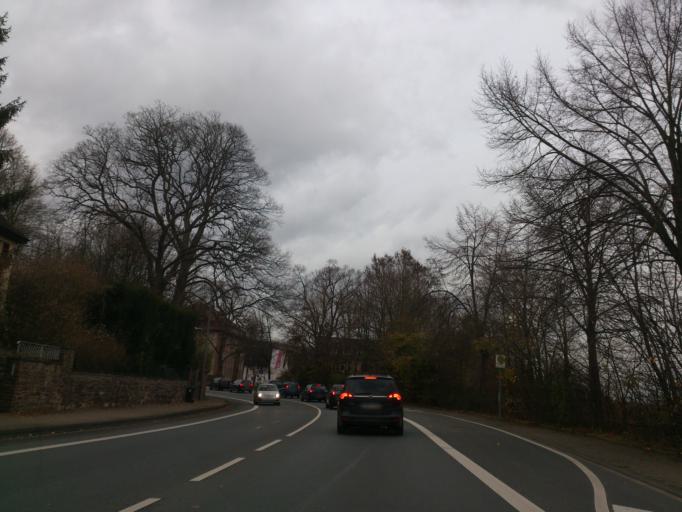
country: DE
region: North Rhine-Westphalia
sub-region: Regierungsbezirk Detmold
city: Hoexter
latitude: 51.7690
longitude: 9.3787
